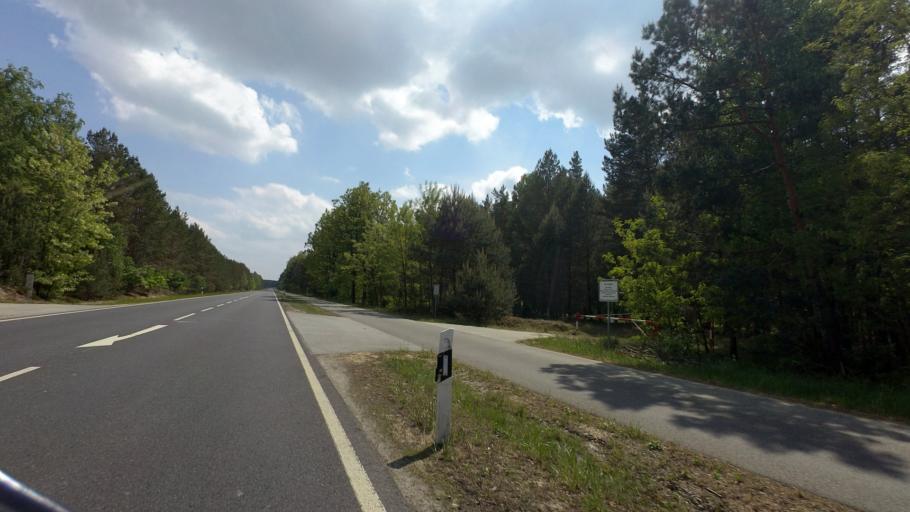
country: DE
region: Saxony
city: Rietschen
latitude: 51.4453
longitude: 14.7750
